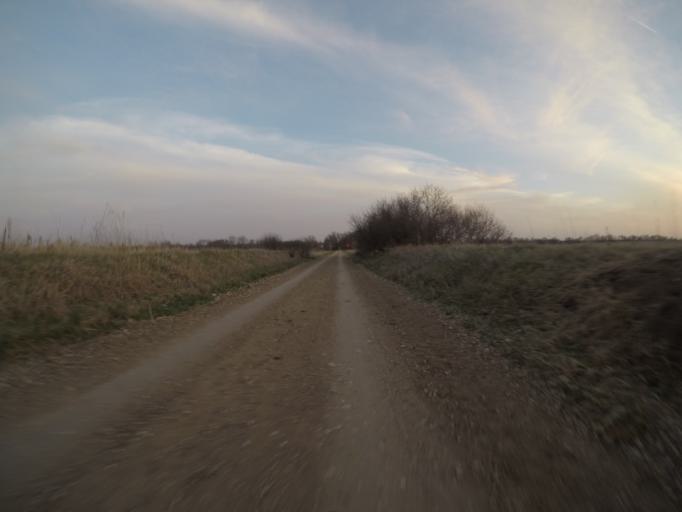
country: US
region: Kansas
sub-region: Riley County
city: Ogden
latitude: 39.1642
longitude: -96.6679
